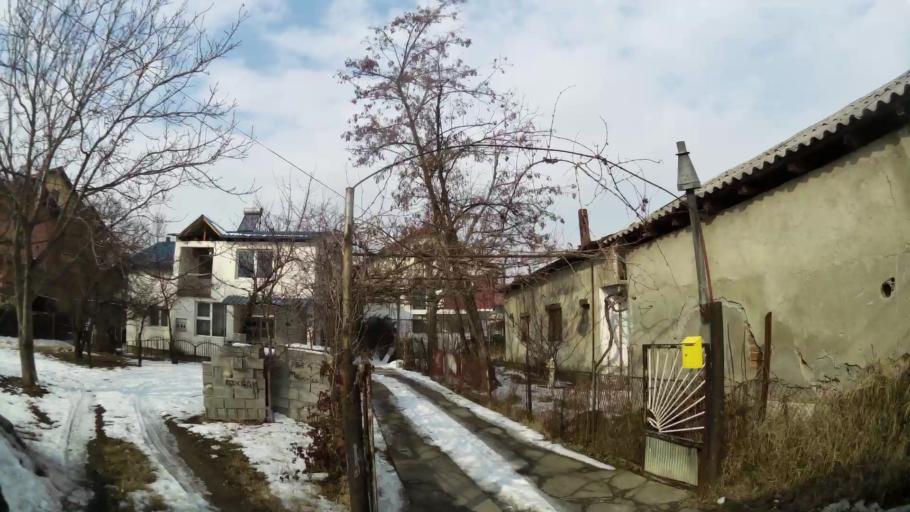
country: MK
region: Saraj
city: Saraj
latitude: 42.0147
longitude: 21.3582
